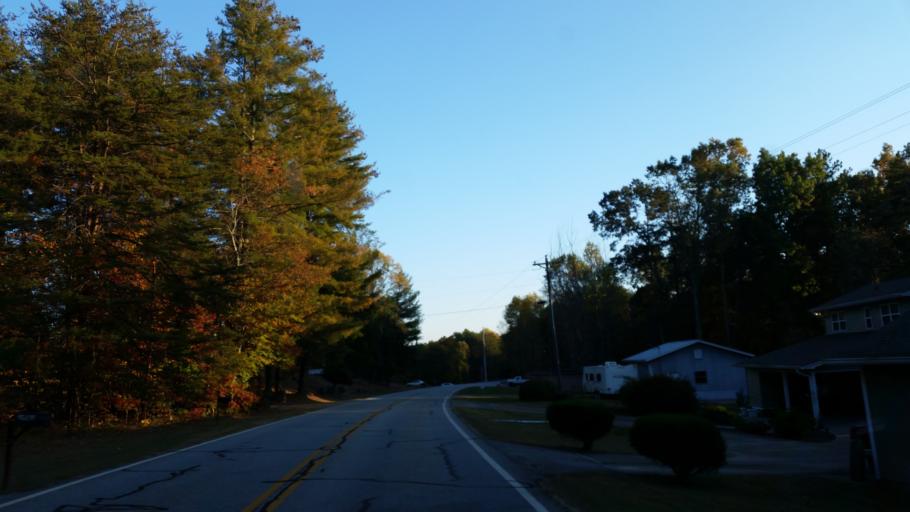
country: US
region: Georgia
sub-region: Lumpkin County
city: Dahlonega
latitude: 34.5400
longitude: -84.0737
